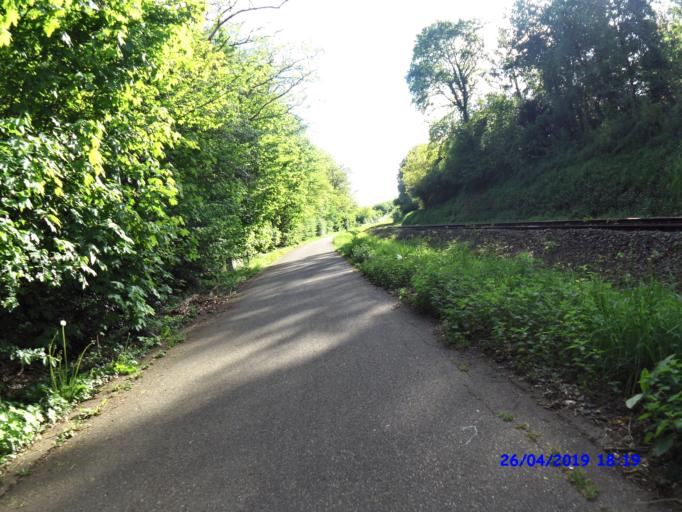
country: BE
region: Flanders
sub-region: Provincie Vlaams-Brabant
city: Diest
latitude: 50.9927
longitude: 5.0679
